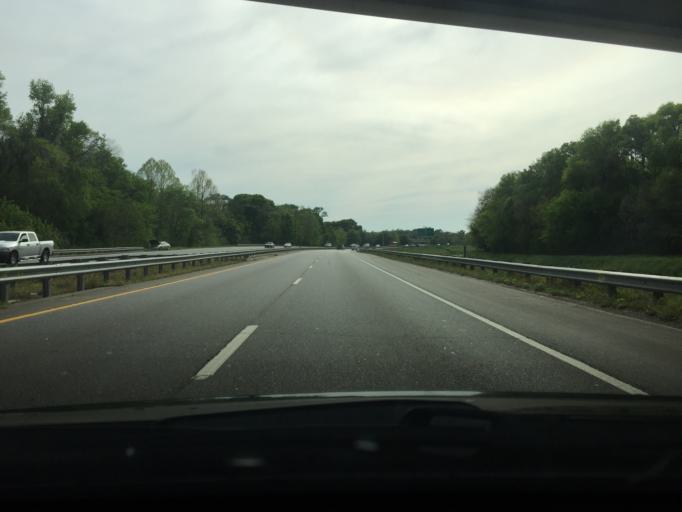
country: US
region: Georgia
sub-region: Chatham County
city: Thunderbolt
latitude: 32.0377
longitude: -81.0766
